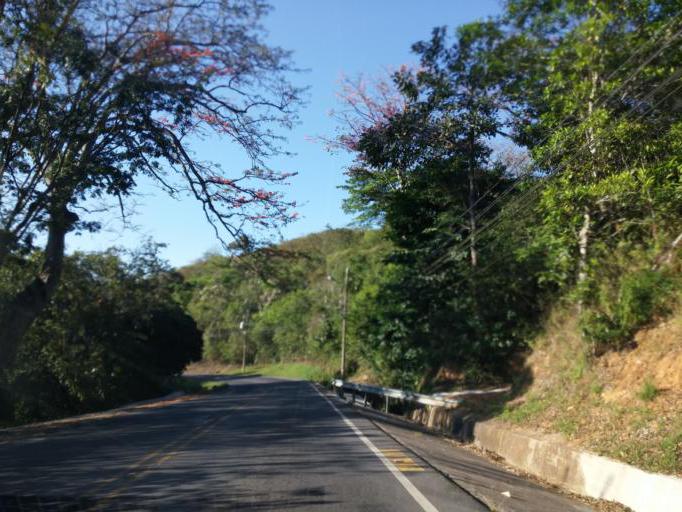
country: CR
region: Heredia
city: Colon
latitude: 9.8901
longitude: -84.2267
